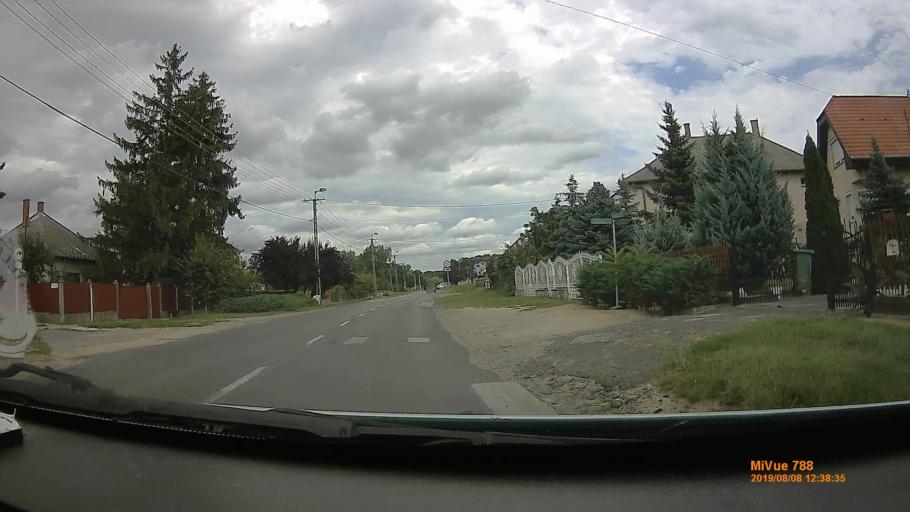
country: HU
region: Szabolcs-Szatmar-Bereg
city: Nyirbator
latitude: 47.8398
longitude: 22.1428
